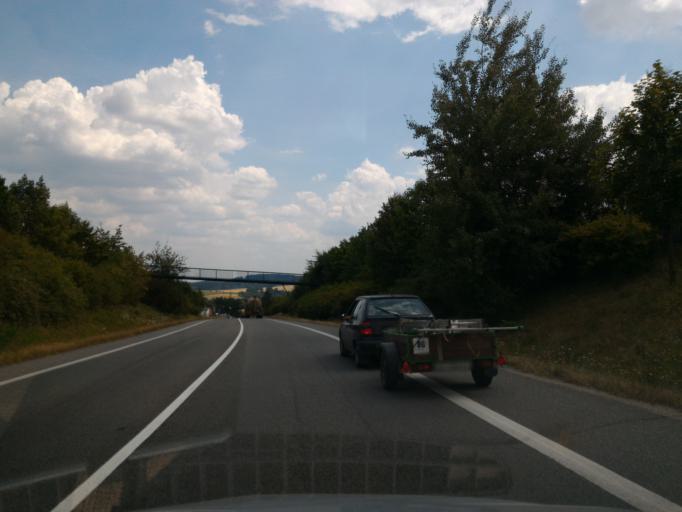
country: CZ
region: Vysocina
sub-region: Okres Havlickuv Brod
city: Havlickuv Brod
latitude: 49.6109
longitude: 15.5929
